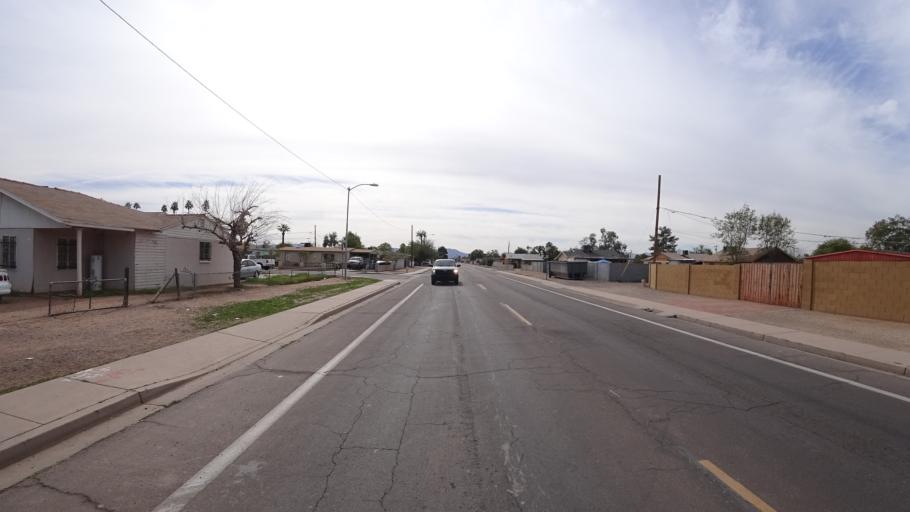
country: US
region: Arizona
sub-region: Maricopa County
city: Phoenix
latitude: 33.4575
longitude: -112.1259
